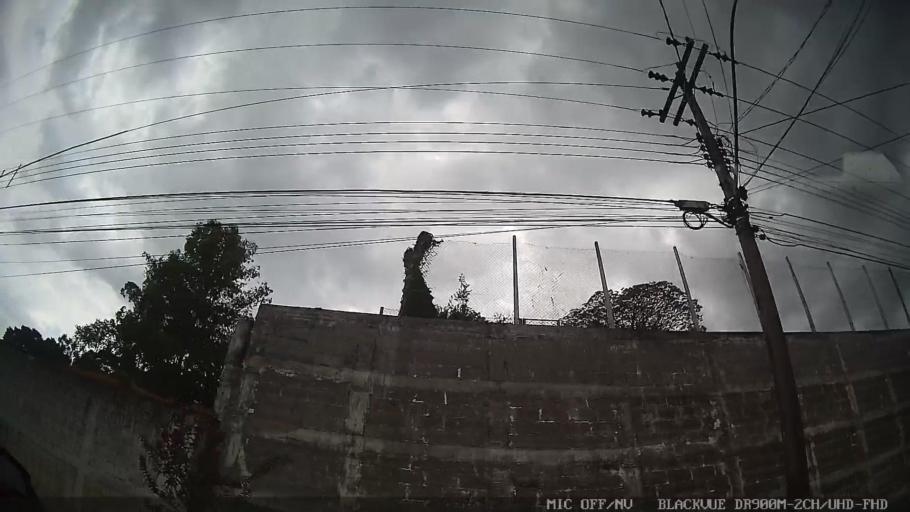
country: BR
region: Sao Paulo
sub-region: Itatiba
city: Itatiba
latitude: -23.0098
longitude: -46.8399
